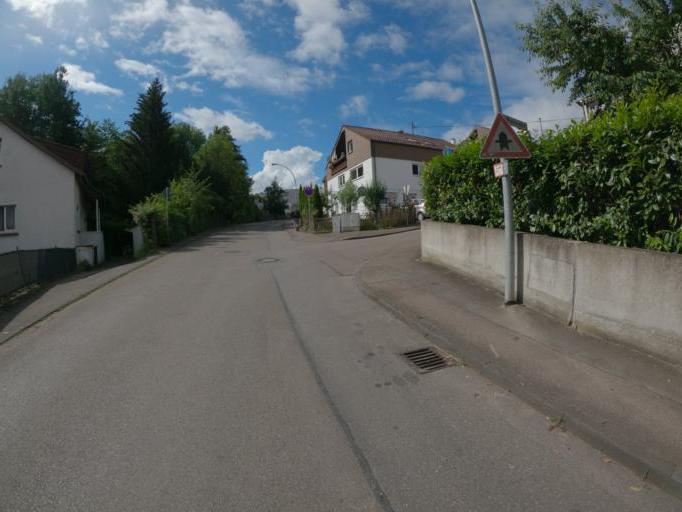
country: DE
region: Baden-Wuerttemberg
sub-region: Regierungsbezirk Stuttgart
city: Ebersbach an der Fils
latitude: 48.7105
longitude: 9.5242
